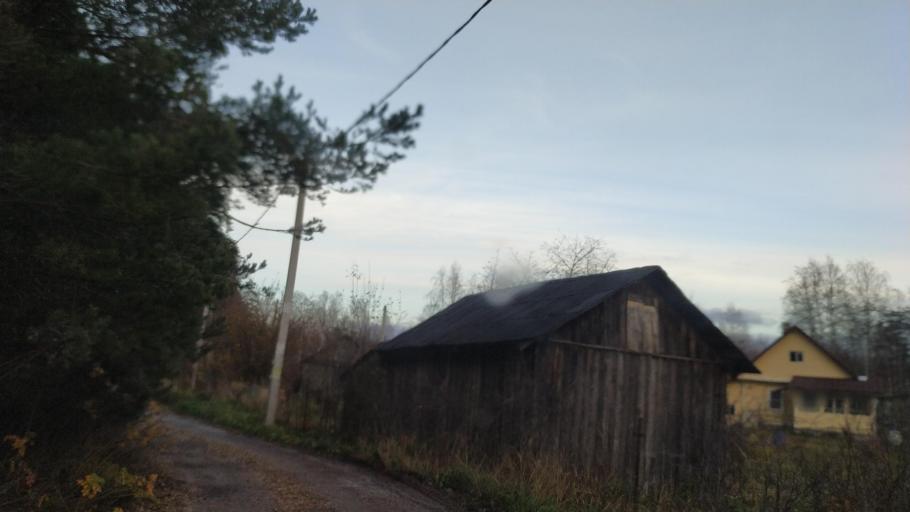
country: RU
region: Leningrad
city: Sosnovyy Bor
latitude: 59.9544
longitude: 29.0967
